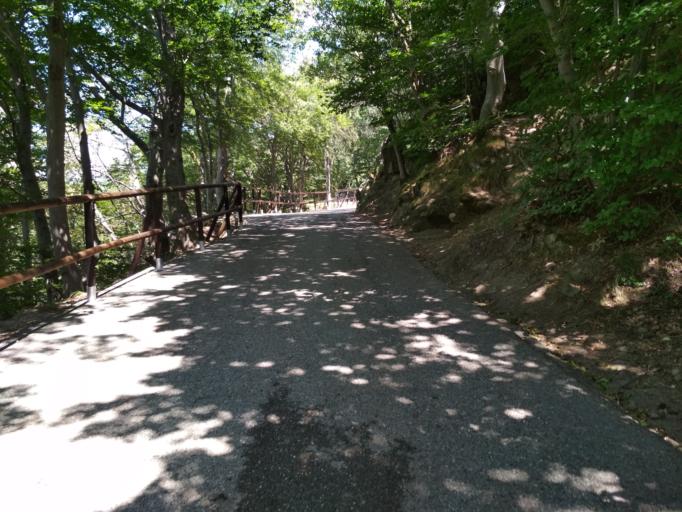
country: IT
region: Piedmont
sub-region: Provincia di Torino
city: Chiusa di San Michele
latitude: 45.0943
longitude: 7.3394
